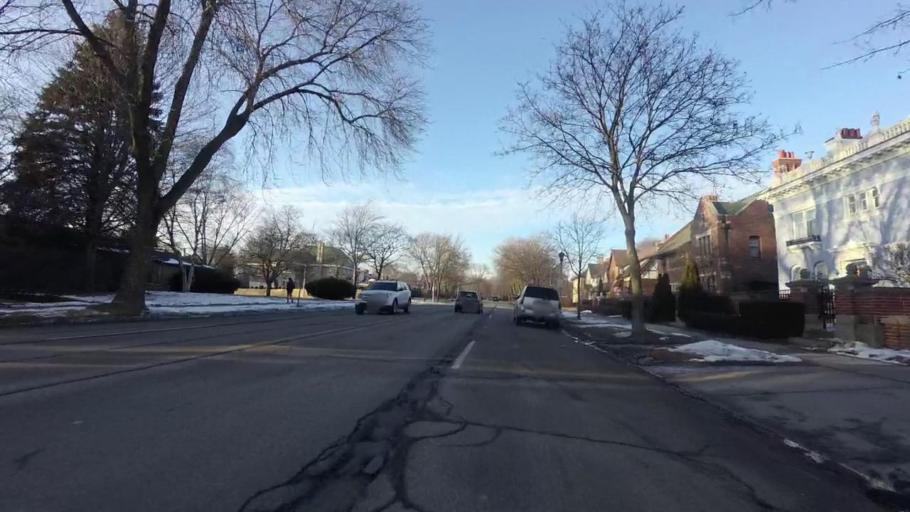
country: US
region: Wisconsin
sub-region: Milwaukee County
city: Shorewood
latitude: 43.0937
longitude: -87.8762
